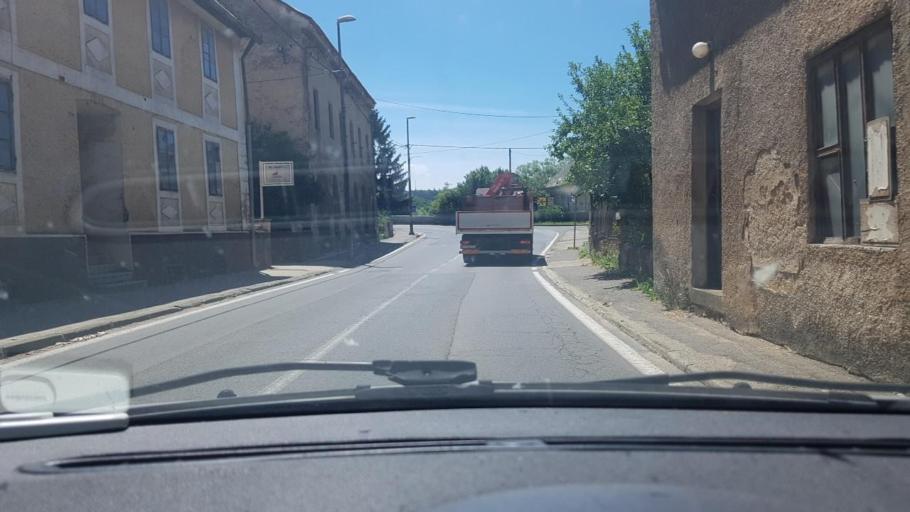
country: HR
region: Licko-Senjska
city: Otocac
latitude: 44.8704
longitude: 15.2299
